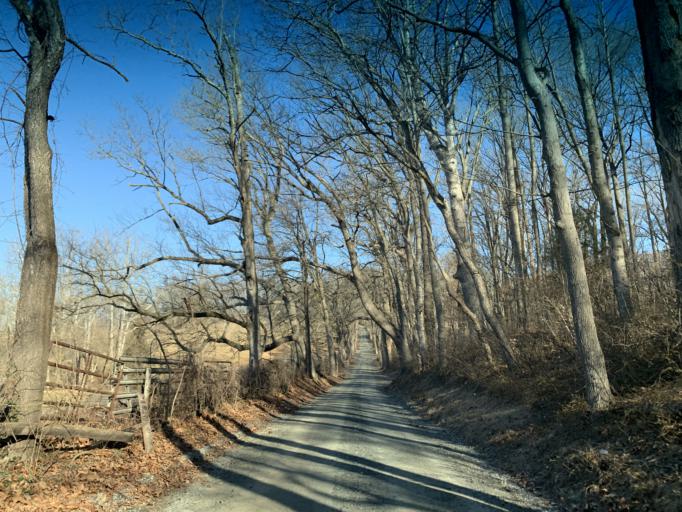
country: US
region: Maryland
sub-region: Harford County
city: Aberdeen
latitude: 39.6087
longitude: -76.2344
